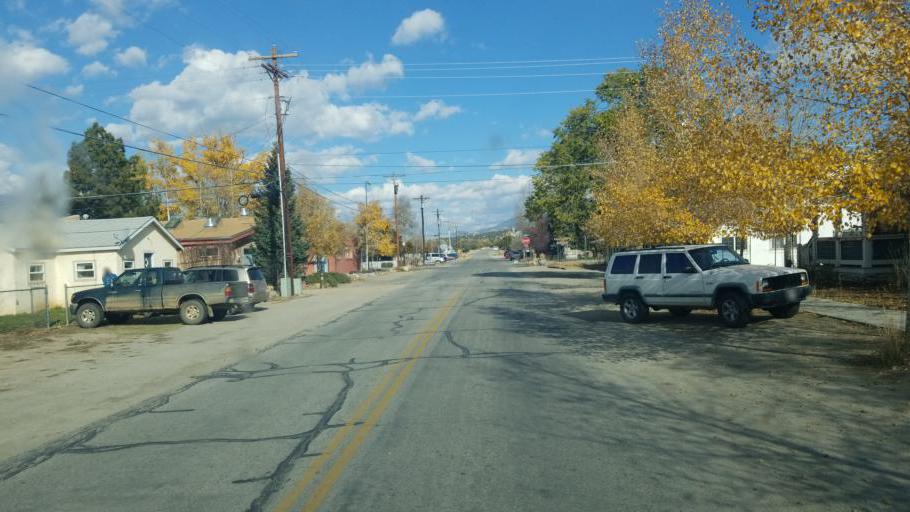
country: US
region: Colorado
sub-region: Chaffee County
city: Buena Vista
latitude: 38.8425
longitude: -106.1273
